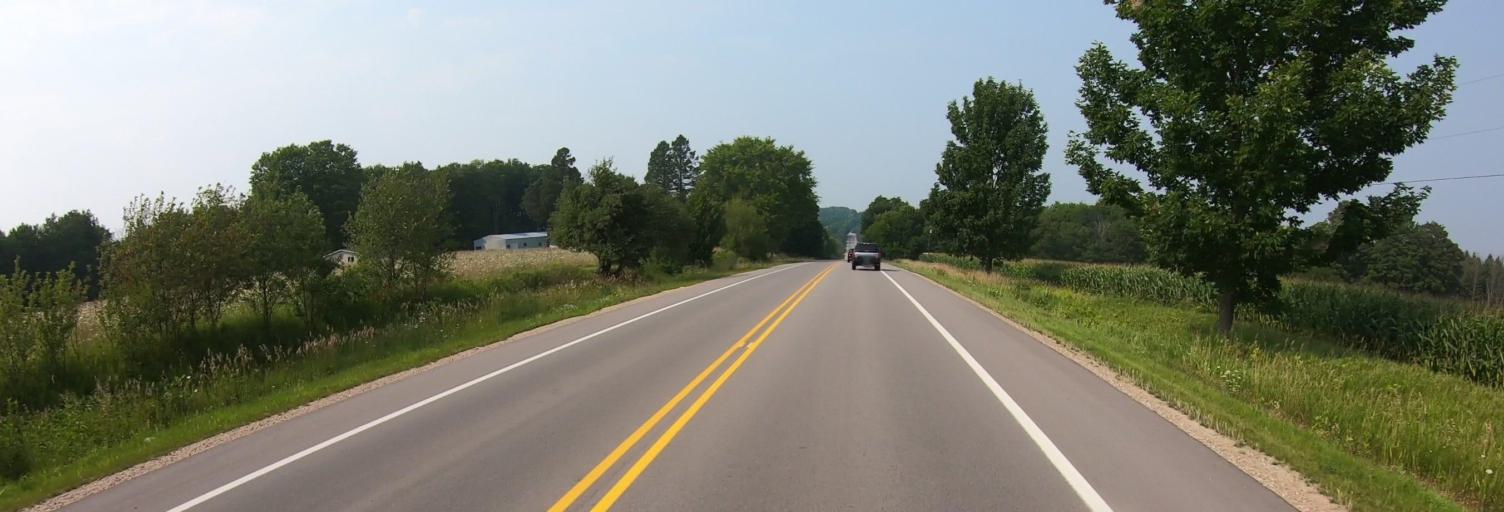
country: US
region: Michigan
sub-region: Charlevoix County
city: Charlevoix
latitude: 45.2448
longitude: -85.2611
